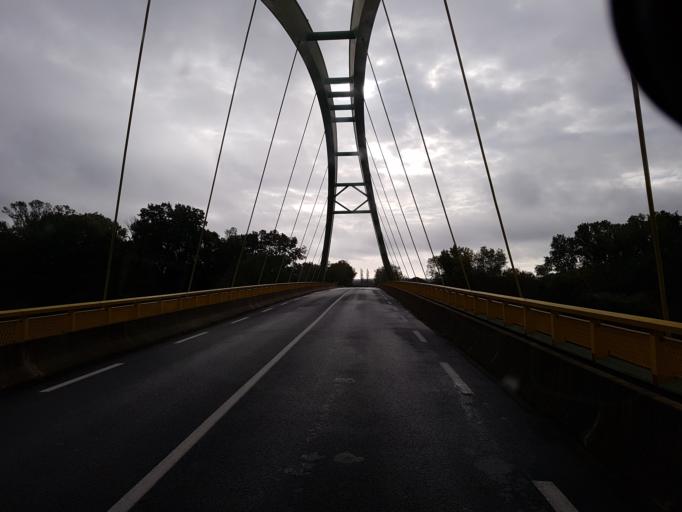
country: FR
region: Languedoc-Roussillon
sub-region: Departement du Gard
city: Saint-Gilles
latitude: 43.6661
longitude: 4.4526
